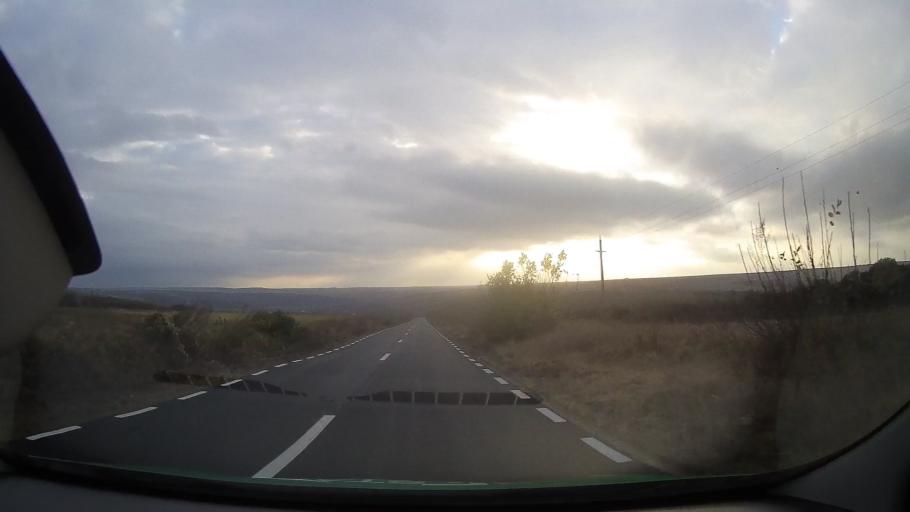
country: RO
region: Constanta
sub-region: Comuna Adamclisi
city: Adamclisi
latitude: 44.0628
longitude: 27.9703
